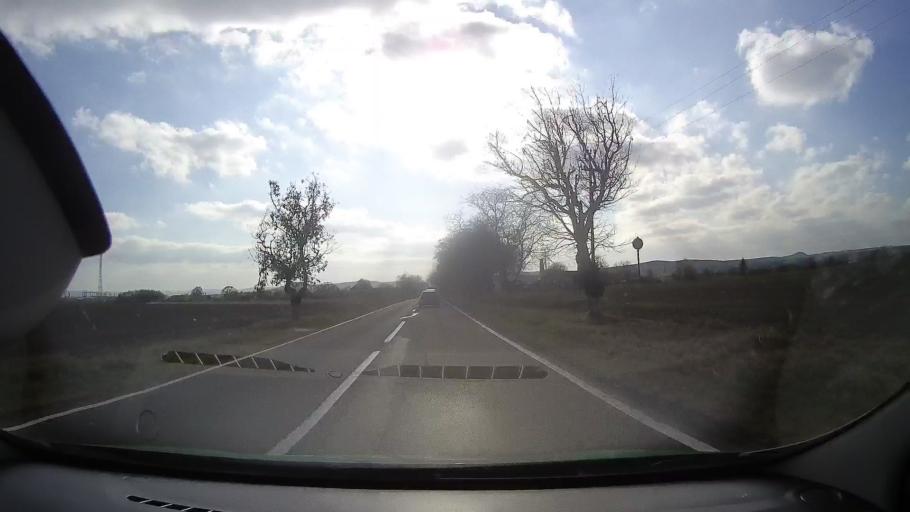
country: RO
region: Tulcea
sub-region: Comuna Nalbant
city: Nalbant
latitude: 45.0546
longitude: 28.6189
